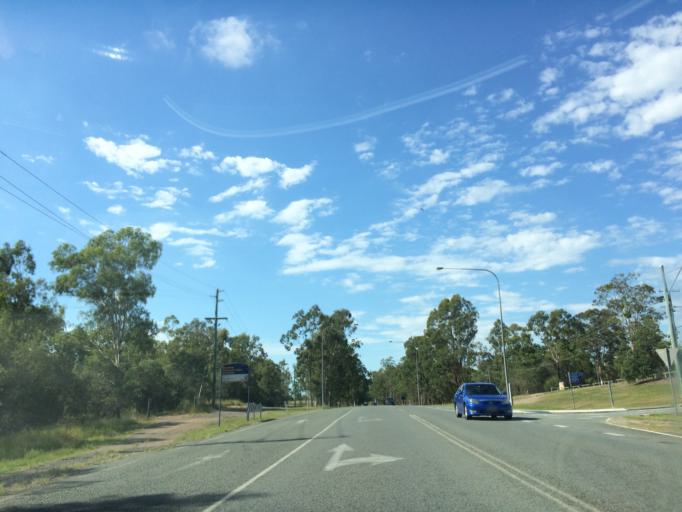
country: AU
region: Queensland
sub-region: Logan
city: Park Ridge South
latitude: -27.7296
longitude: 152.9842
